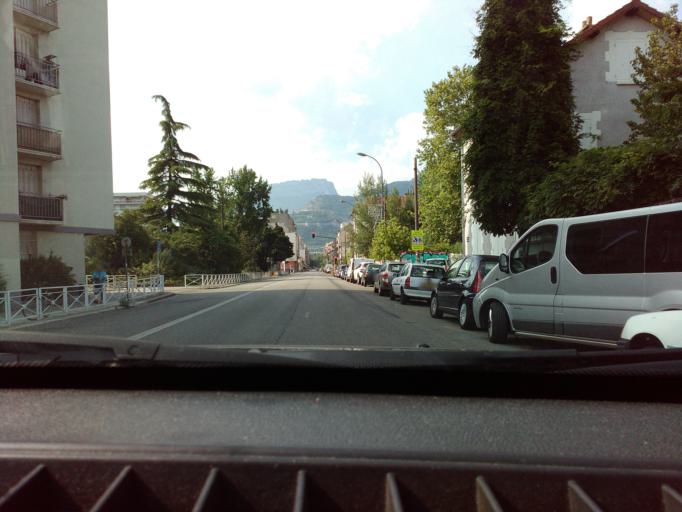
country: FR
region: Rhone-Alpes
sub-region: Departement de l'Isere
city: Grenoble
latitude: 45.1763
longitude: 5.7371
